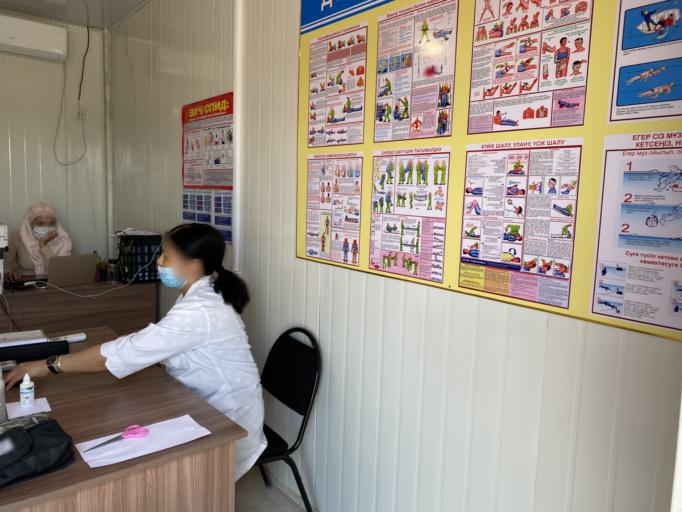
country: KZ
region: Qaraghandy
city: Balqash
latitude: 46.6439
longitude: 74.3938
